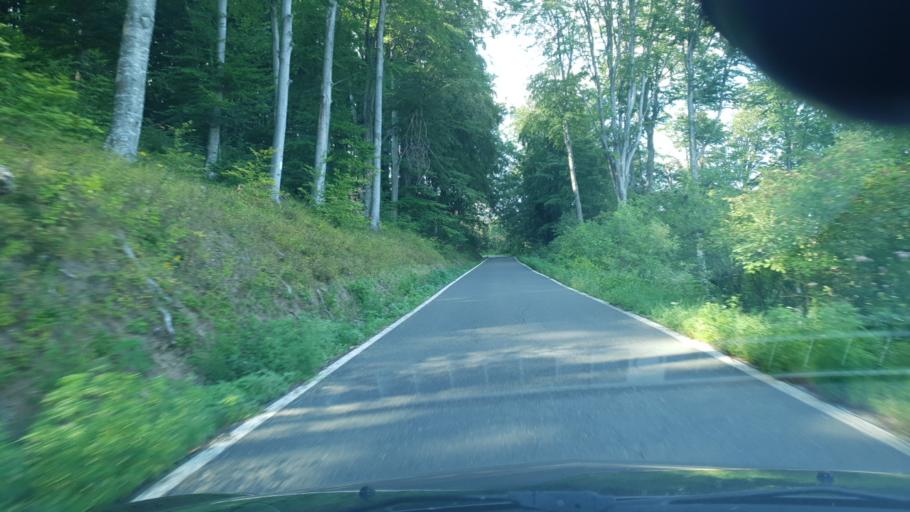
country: HR
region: Grad Zagreb
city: Kasina
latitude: 45.8862
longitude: 15.9678
